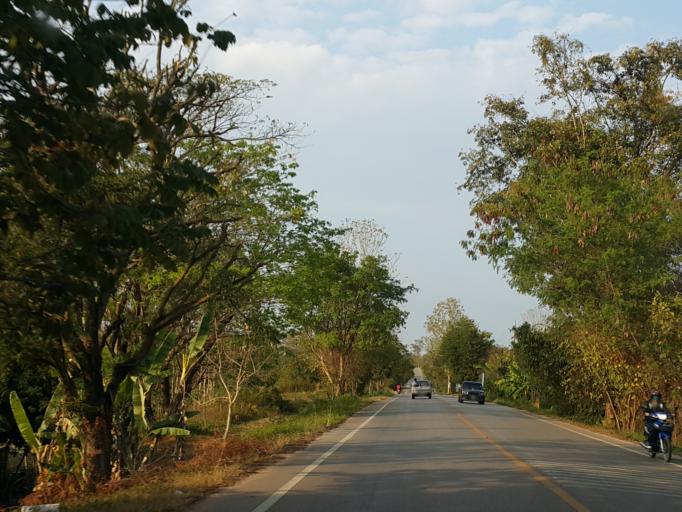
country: TH
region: Lampang
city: Lampang
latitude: 18.5061
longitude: 99.4735
